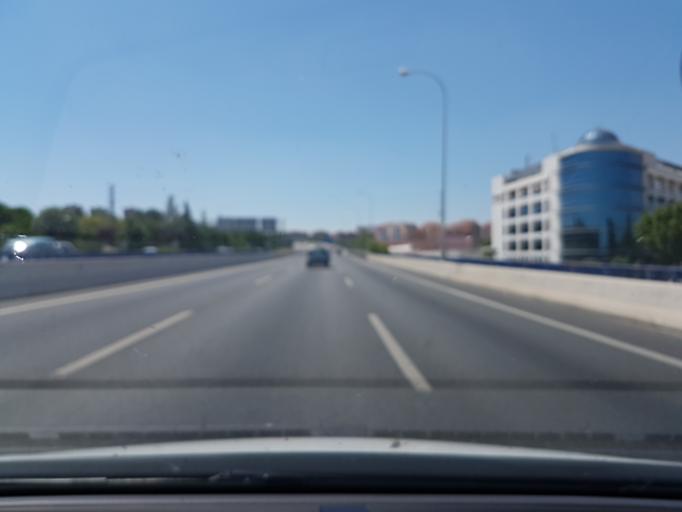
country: ES
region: Madrid
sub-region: Provincia de Madrid
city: Villaverde
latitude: 40.3620
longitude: -3.6839
